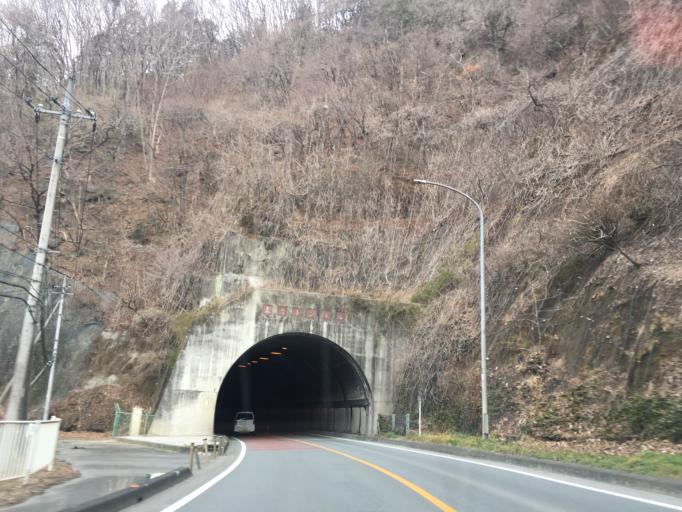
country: JP
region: Saitama
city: Chichibu
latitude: 35.9730
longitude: 139.1595
